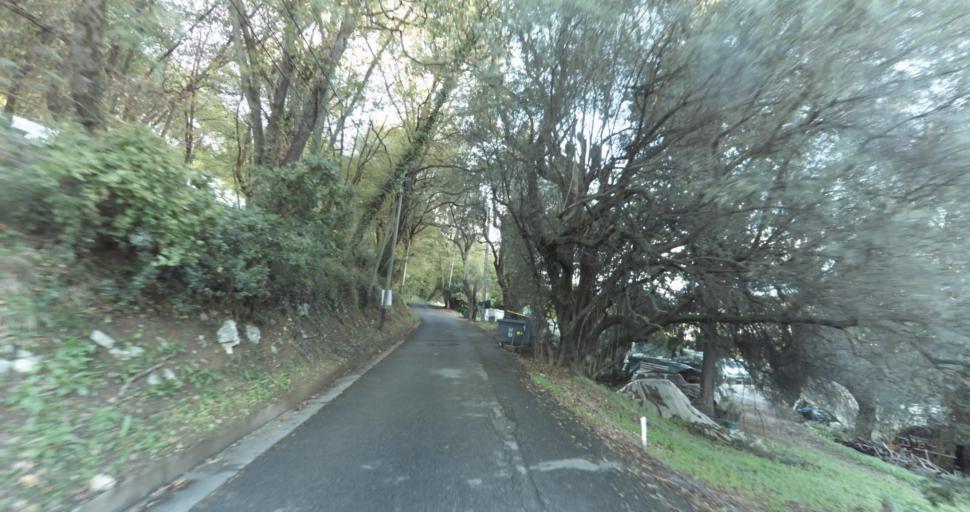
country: FR
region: Provence-Alpes-Cote d'Azur
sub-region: Departement des Alpes-Maritimes
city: La Gaude
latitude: 43.7169
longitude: 7.1360
